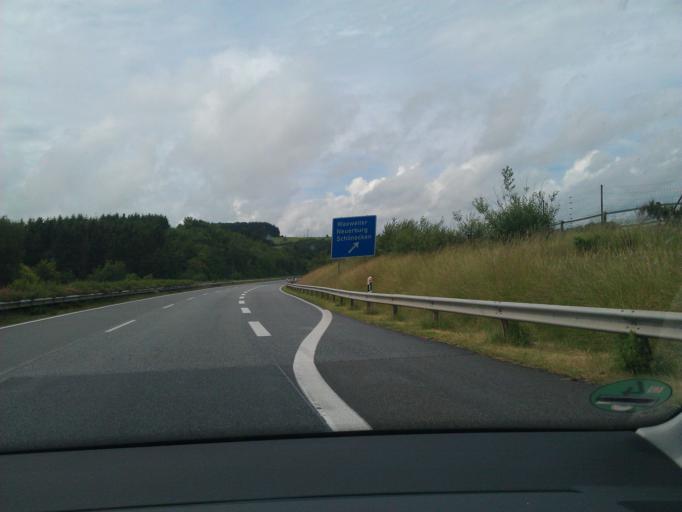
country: DE
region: Rheinland-Pfalz
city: Feuerscheid
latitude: 50.0929
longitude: 6.4497
